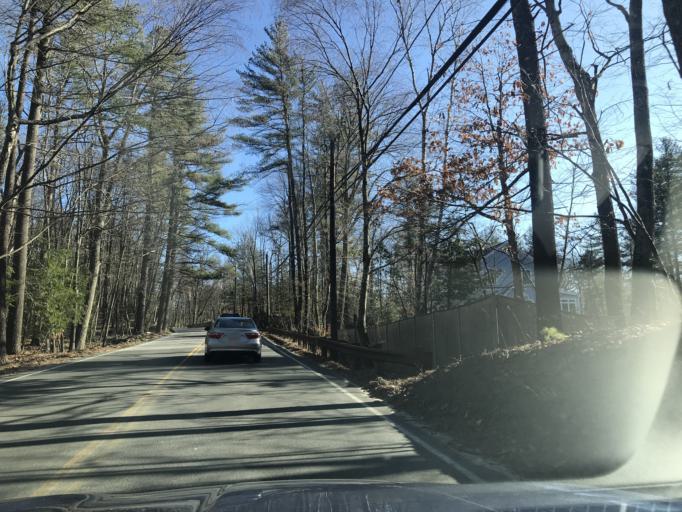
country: US
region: Massachusetts
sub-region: Essex County
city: Groveland
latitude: 42.7123
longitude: -71.0445
